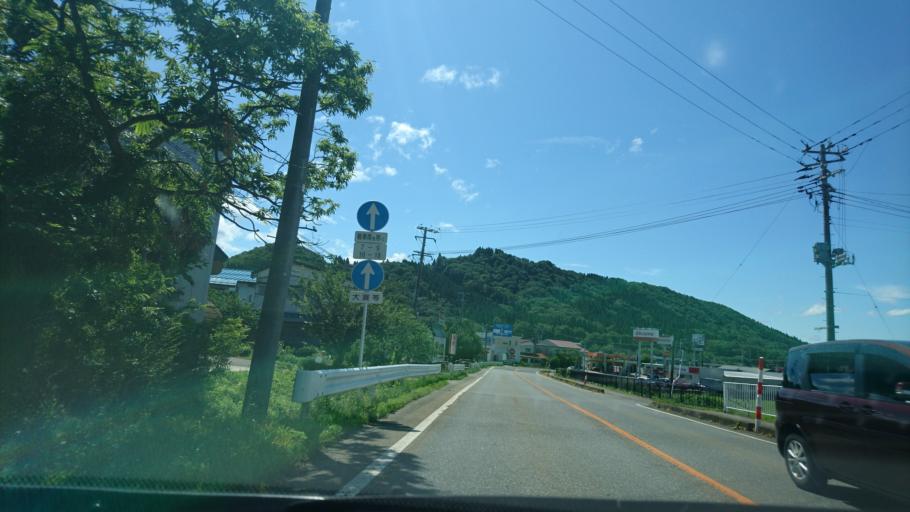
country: JP
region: Akita
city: Kakunodatemachi
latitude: 39.5958
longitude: 140.5760
